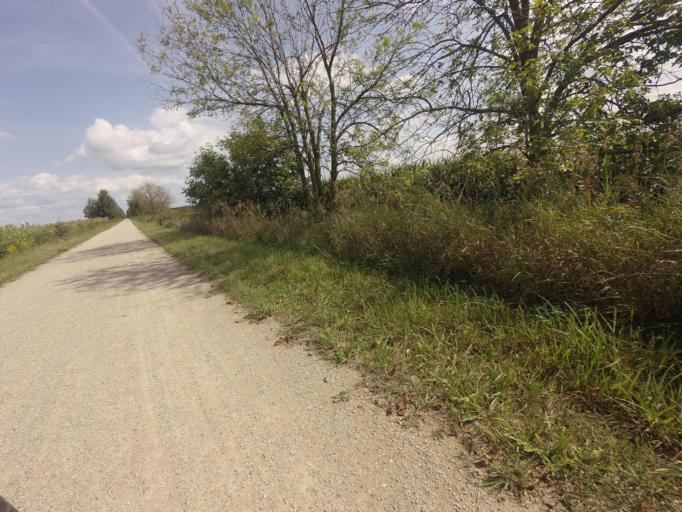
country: CA
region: Ontario
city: Waterloo
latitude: 43.5815
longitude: -80.7476
